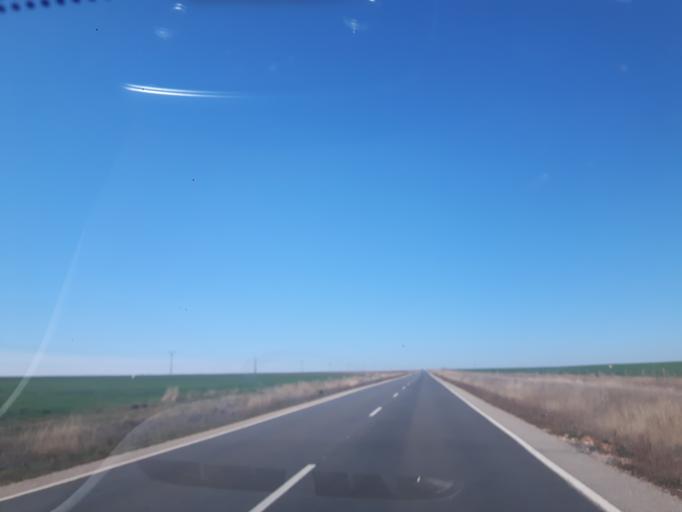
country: ES
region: Castille and Leon
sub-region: Provincia de Salamanca
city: Nava de Sotrobal
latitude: 40.8848
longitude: -5.3100
